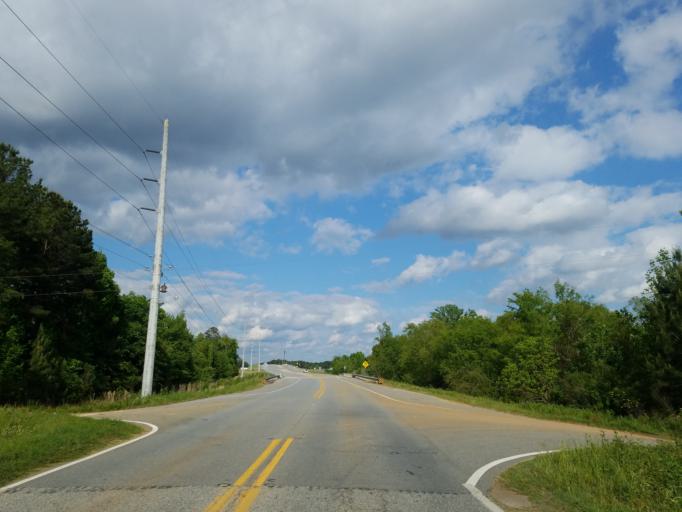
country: US
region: Georgia
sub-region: Crisp County
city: Cordele
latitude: 32.0040
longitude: -83.7644
